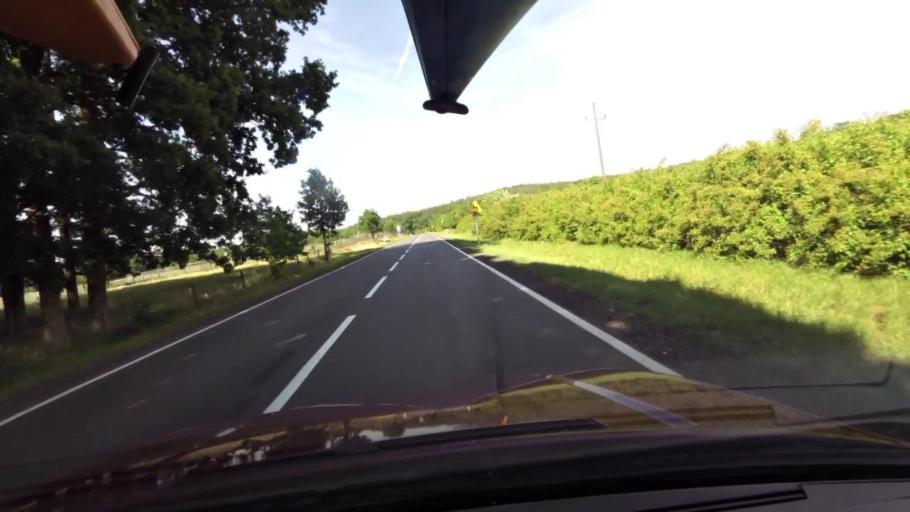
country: PL
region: Pomeranian Voivodeship
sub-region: Powiat bytowski
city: Miastko
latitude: 54.1098
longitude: 16.9927
